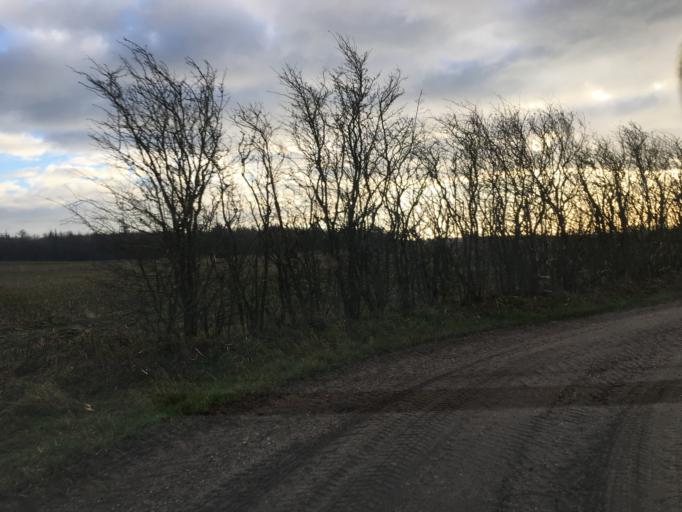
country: DK
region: South Denmark
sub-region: Tonder Kommune
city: Logumkloster
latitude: 55.1184
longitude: 8.8817
